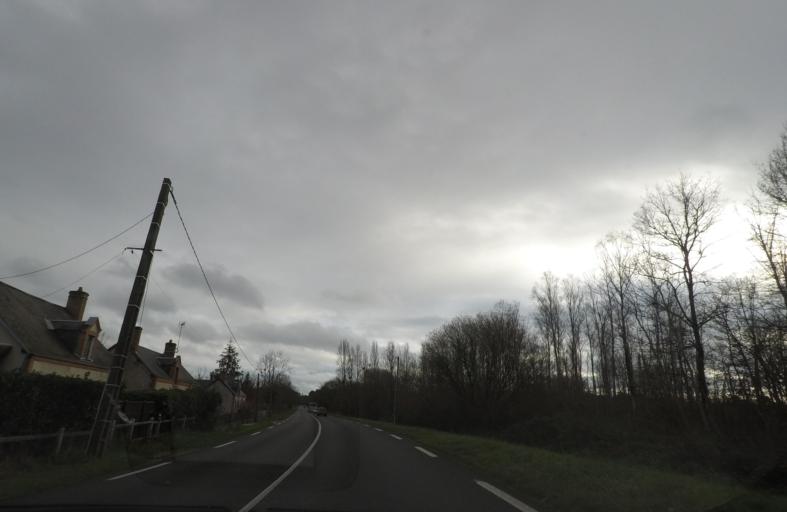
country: FR
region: Centre
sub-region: Departement du Loir-et-Cher
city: Mur-de-Sologne
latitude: 47.4069
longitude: 1.6170
